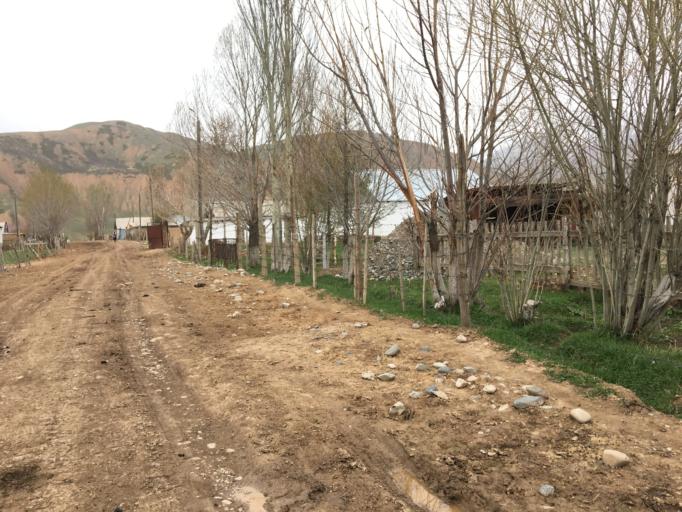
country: KG
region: Naryn
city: Naryn
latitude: 41.5193
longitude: 76.4403
